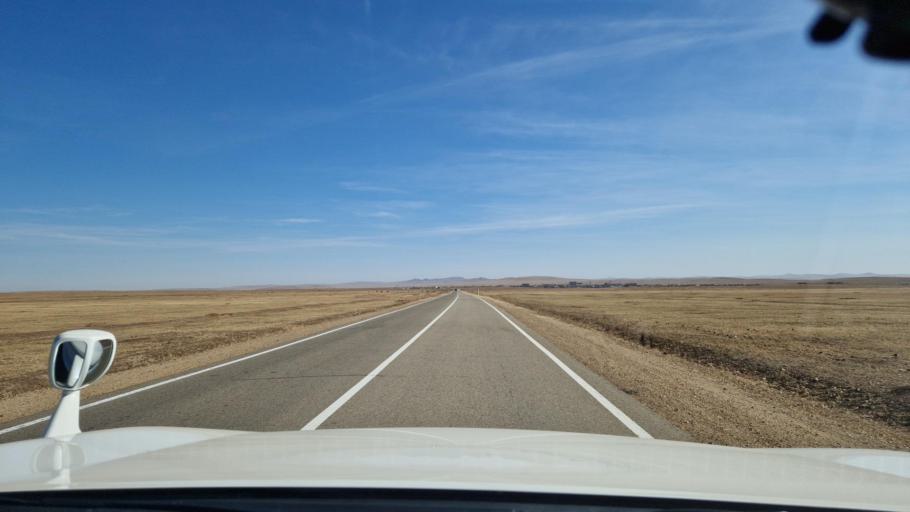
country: MN
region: Suhbaatar
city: Hanhohiy
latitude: 47.5720
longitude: 112.3131
